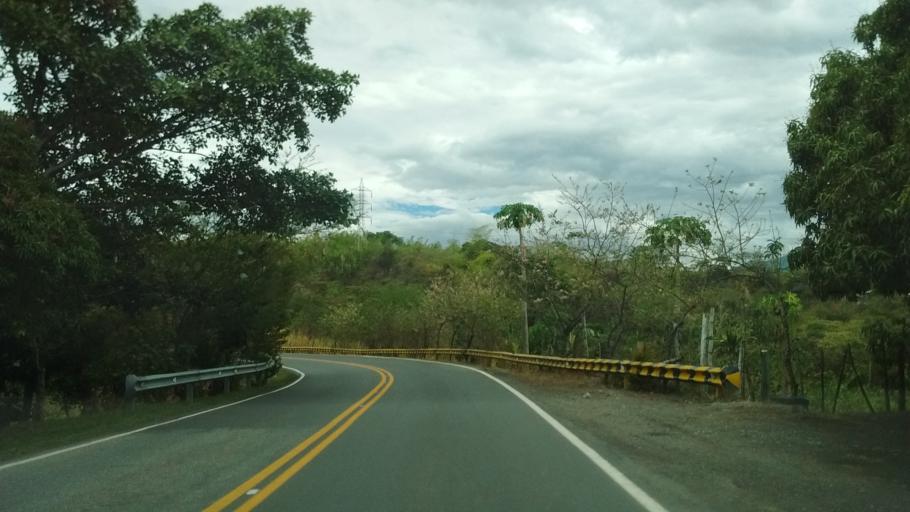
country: CO
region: Cauca
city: La Sierra
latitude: 2.2301
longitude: -76.7942
